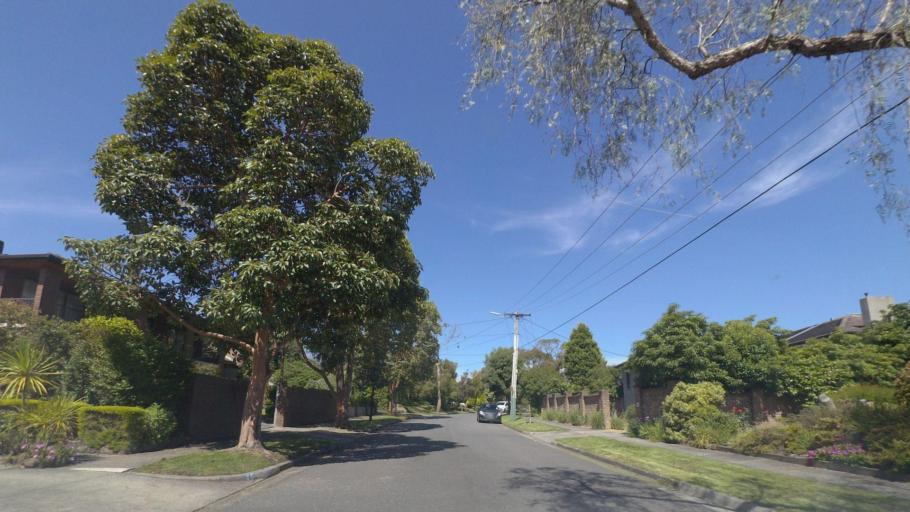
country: AU
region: Victoria
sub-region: Whitehorse
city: Vermont South
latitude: -37.8529
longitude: 145.1988
